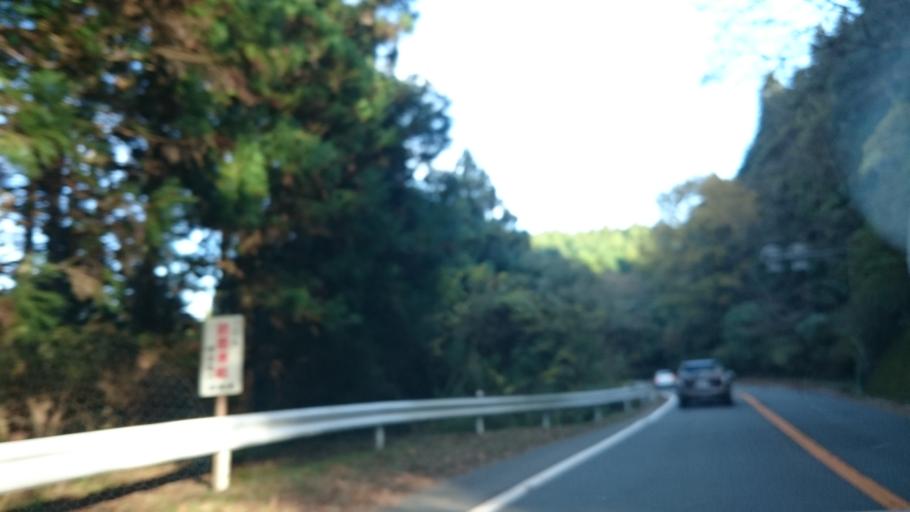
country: JP
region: Shizuoka
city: Heda
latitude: 34.9755
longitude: 138.8660
